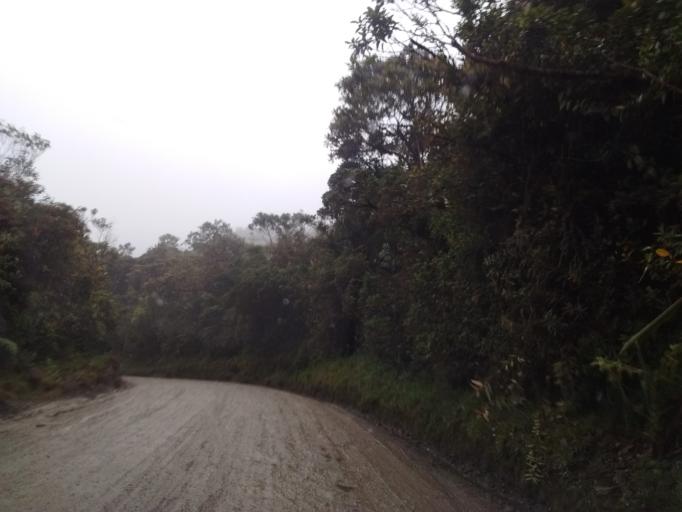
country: CO
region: Cauca
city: Paispamba
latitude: 2.1543
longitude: -76.4507
